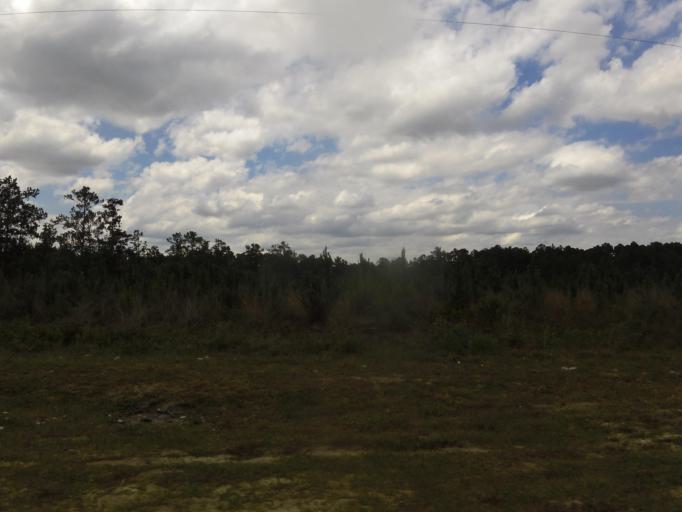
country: US
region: Florida
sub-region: Clay County
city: Green Cove Springs
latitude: 29.9150
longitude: -81.7800
